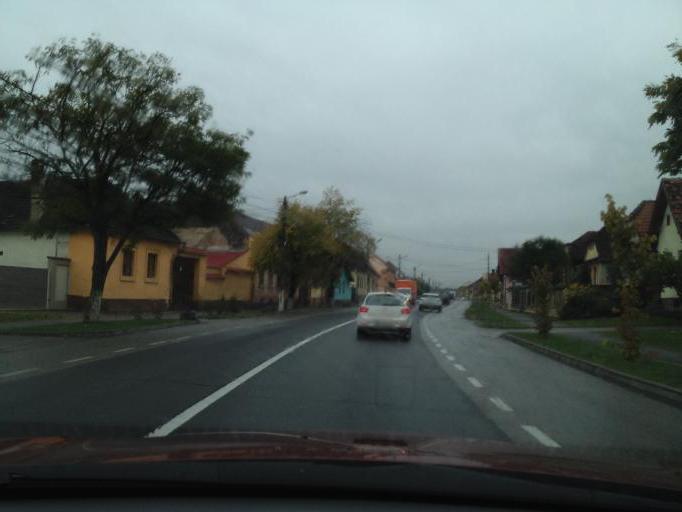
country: RO
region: Brasov
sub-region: Comuna Cristian
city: Cristian
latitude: 45.6280
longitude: 25.4846
